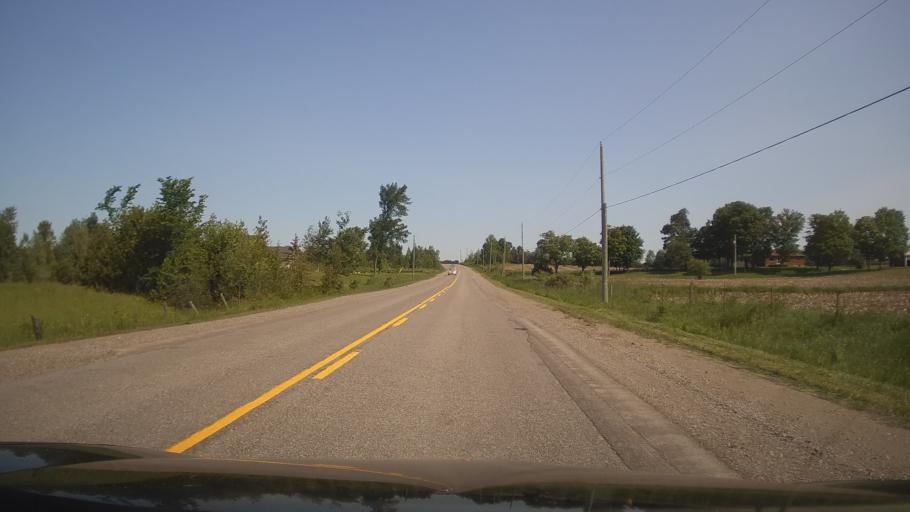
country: CA
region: Ontario
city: Omemee
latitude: 44.4511
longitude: -78.9267
